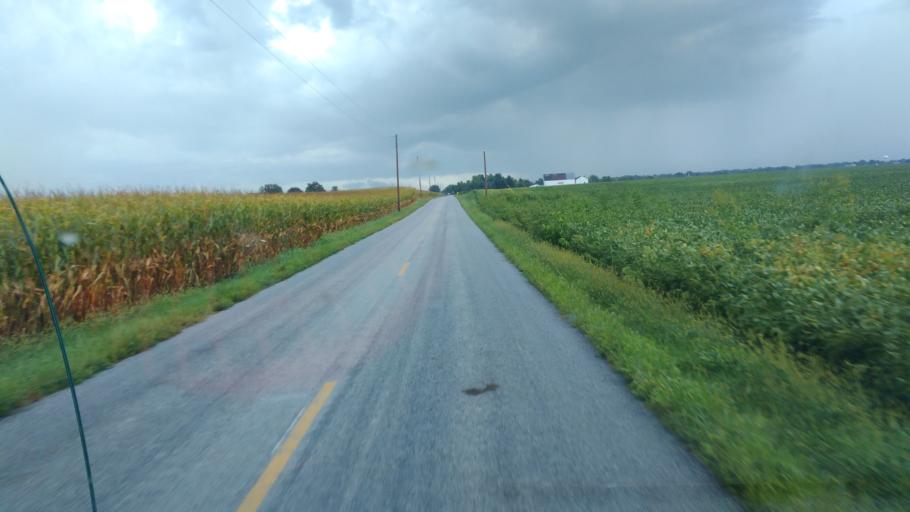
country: US
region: Ohio
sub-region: Hardin County
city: Kenton
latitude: 40.6821
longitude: -83.5951
